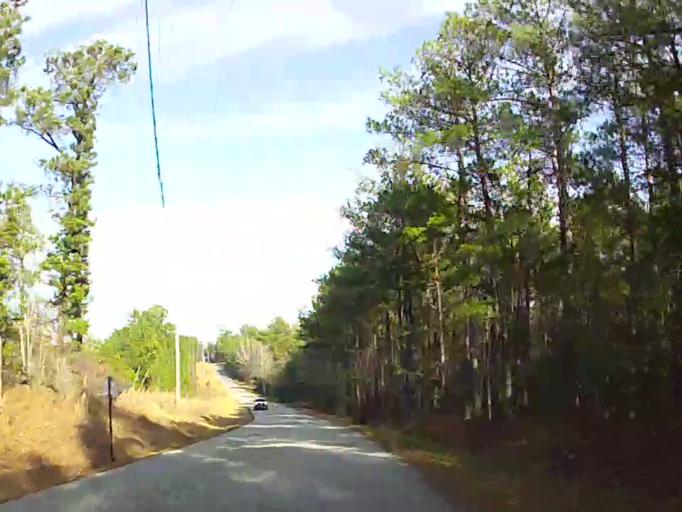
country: US
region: Georgia
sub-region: Monroe County
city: Forsyth
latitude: 32.9821
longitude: -83.7897
